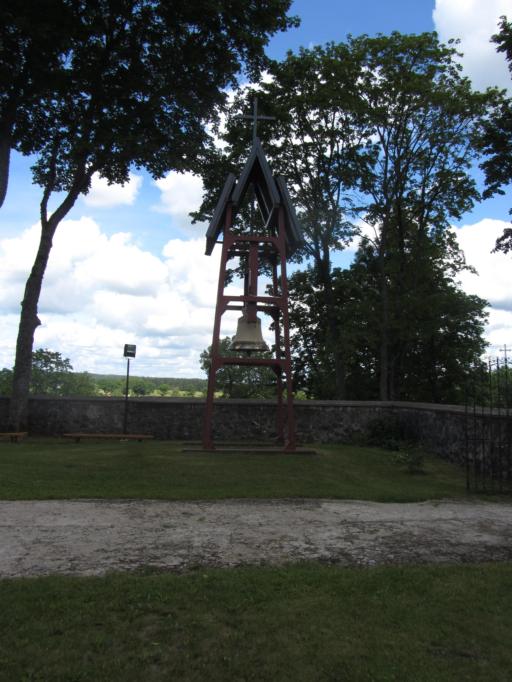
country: LT
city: Svencionys
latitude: 55.0702
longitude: 26.1356
